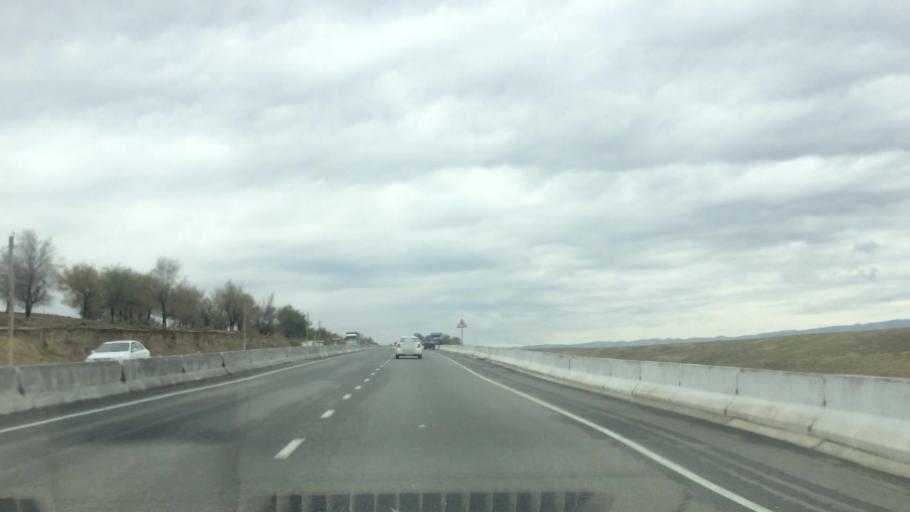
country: UZ
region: Samarqand
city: Bulung'ur
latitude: 39.9470
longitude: 67.5342
